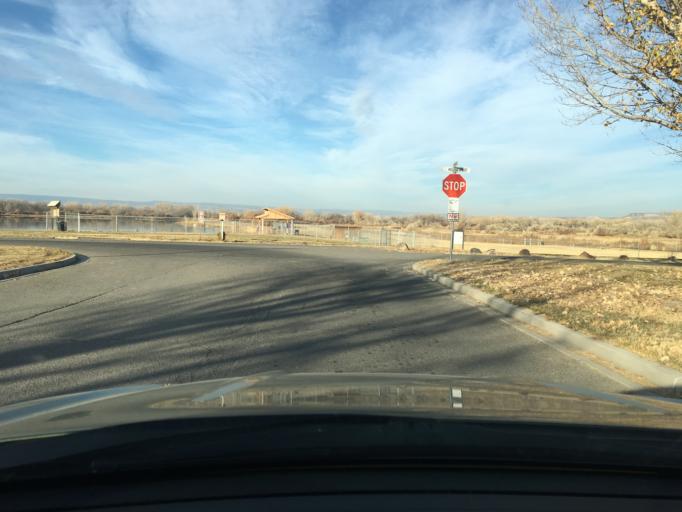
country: US
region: Colorado
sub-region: Delta County
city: Delta
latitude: 38.7516
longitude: -108.0785
